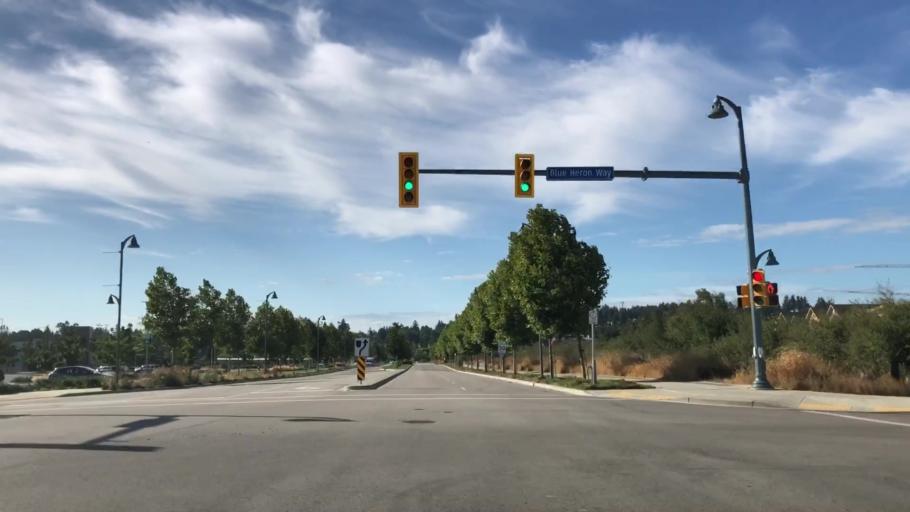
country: CA
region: British Columbia
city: Ladner
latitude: 49.0378
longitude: -123.0903
